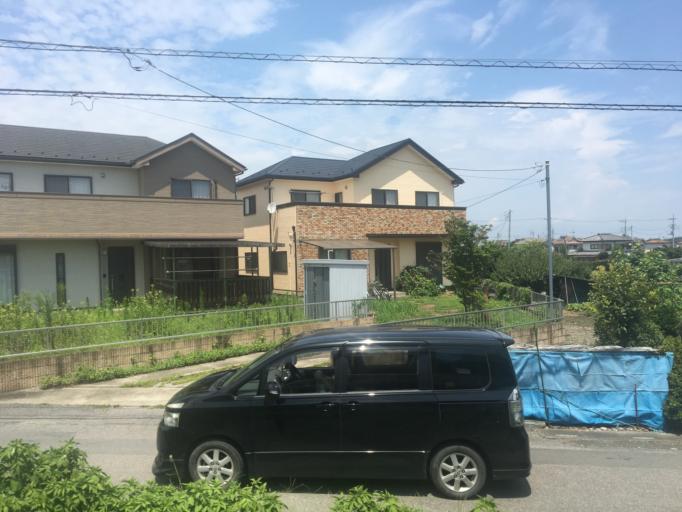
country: JP
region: Saitama
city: Kodamacho-kodamaminami
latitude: 36.1856
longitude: 139.1494
